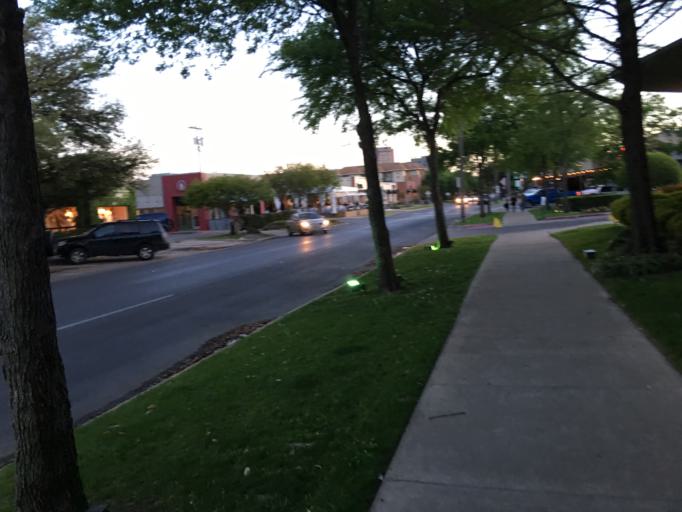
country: US
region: Texas
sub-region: Dallas County
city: Highland Park
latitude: 32.8216
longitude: -96.7883
